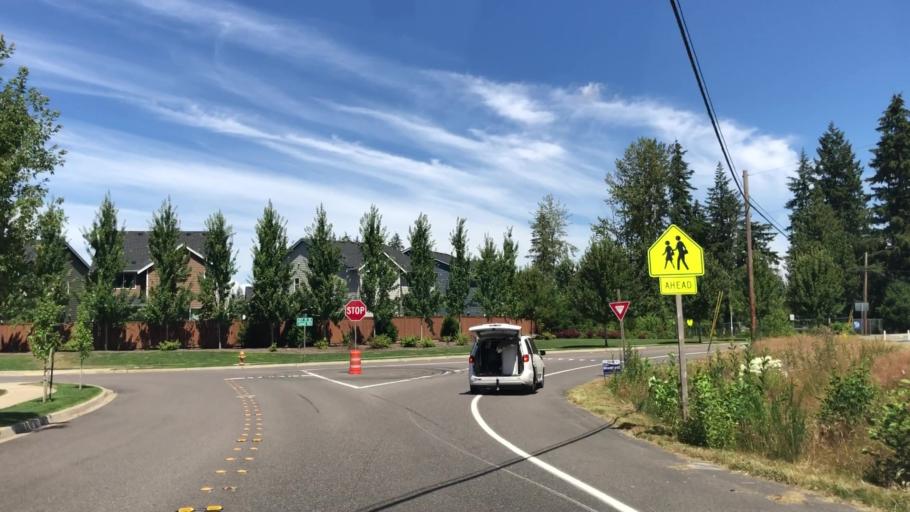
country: US
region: Washington
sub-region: Snohomish County
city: North Creek
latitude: 47.8178
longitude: -122.1815
